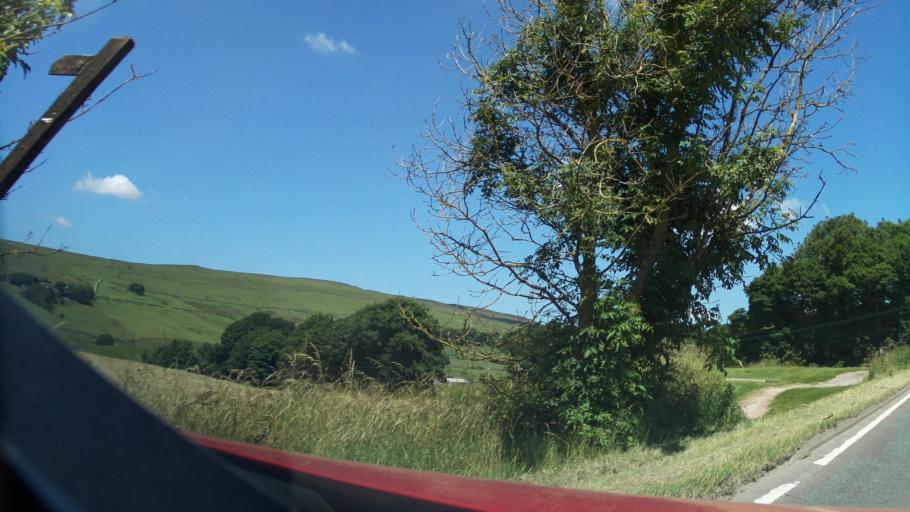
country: GB
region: England
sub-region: Derbyshire
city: Buxton
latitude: 53.2695
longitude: -1.8964
